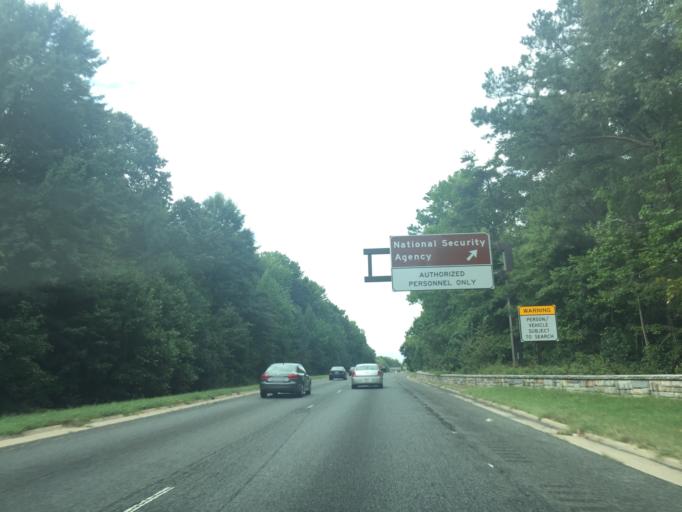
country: US
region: Maryland
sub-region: Howard County
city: Fort George G Mead Junction
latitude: 39.1236
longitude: -76.7671
